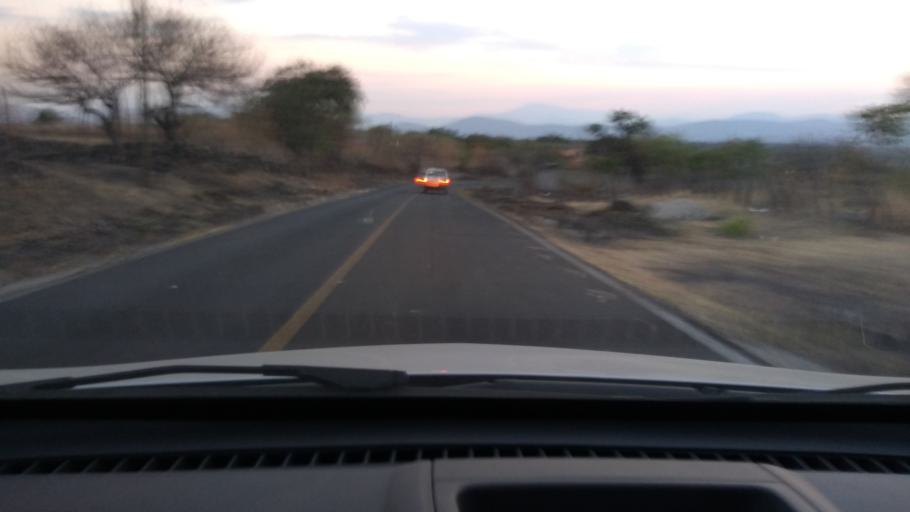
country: MX
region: Morelos
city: Coatetelco
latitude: 18.7222
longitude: -99.3043
